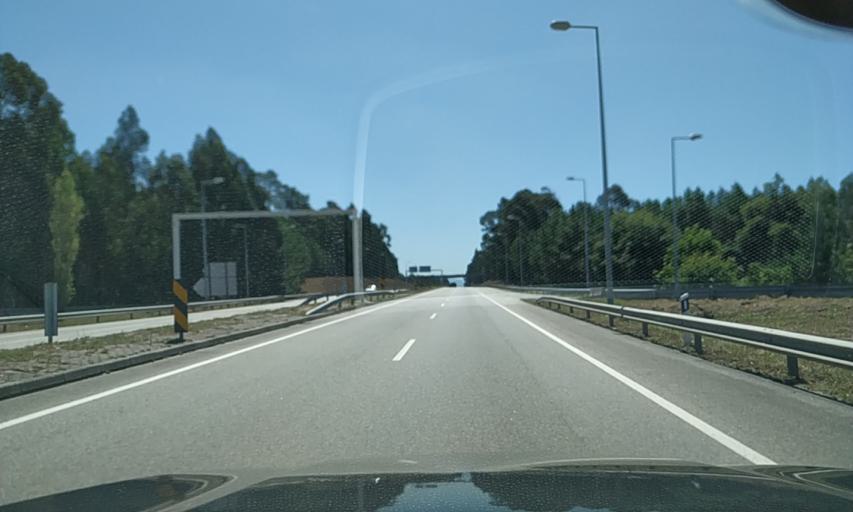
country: PT
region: Aveiro
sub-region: Agueda
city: Agueda
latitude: 40.5535
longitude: -8.4736
